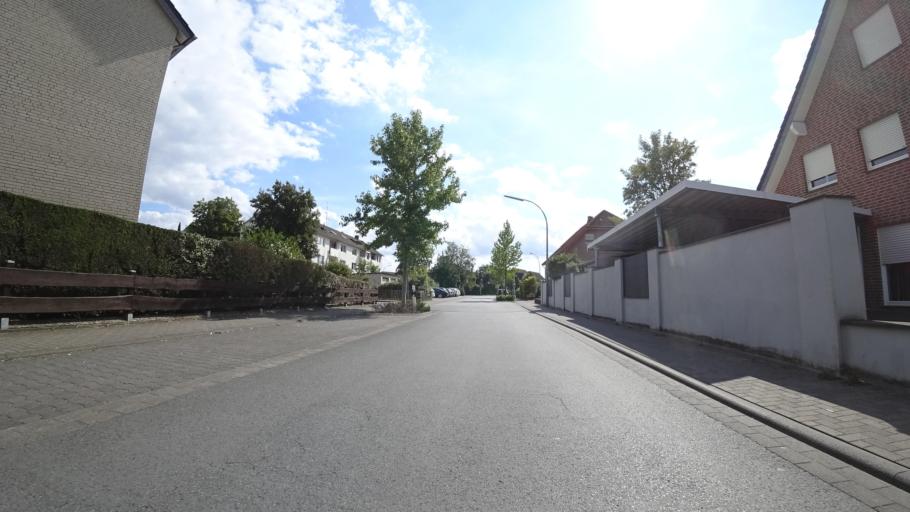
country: DE
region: North Rhine-Westphalia
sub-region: Regierungsbezirk Detmold
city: Rheda-Wiedenbruck
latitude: 51.8441
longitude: 8.3133
